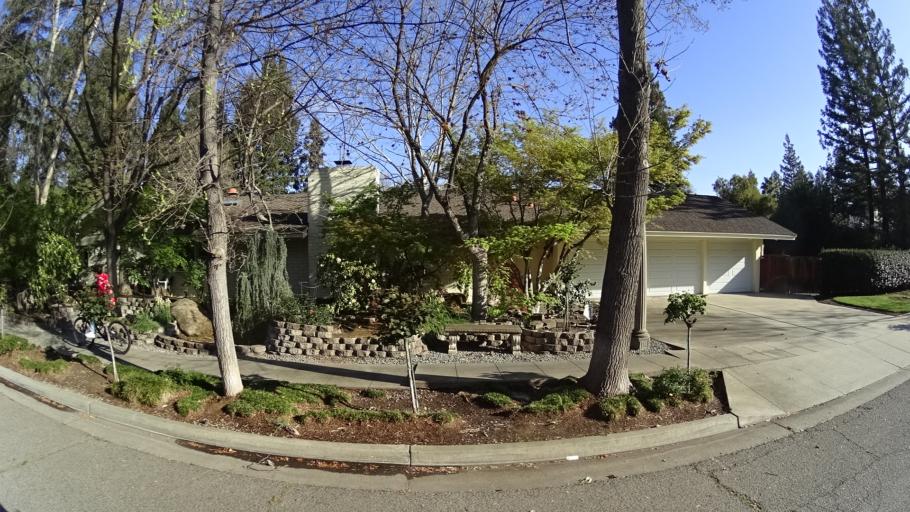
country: US
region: California
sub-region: Fresno County
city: Fresno
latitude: 36.8209
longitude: -119.8347
